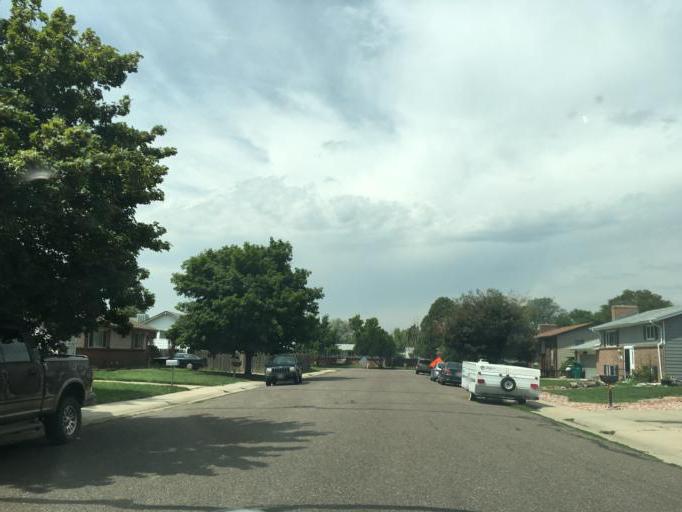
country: US
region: Colorado
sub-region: Adams County
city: Aurora
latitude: 39.7322
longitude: -104.7948
